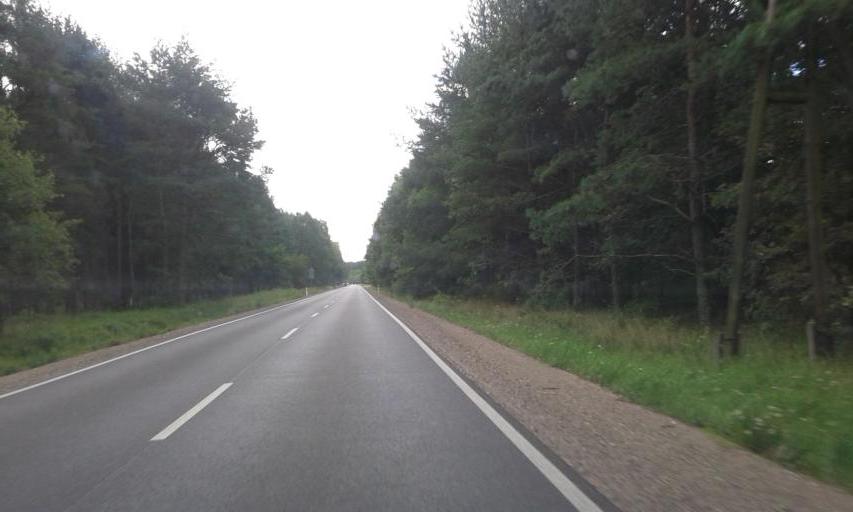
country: PL
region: West Pomeranian Voivodeship
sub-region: Powiat szczecinecki
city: Lubowo
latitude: 53.4713
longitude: 16.3603
